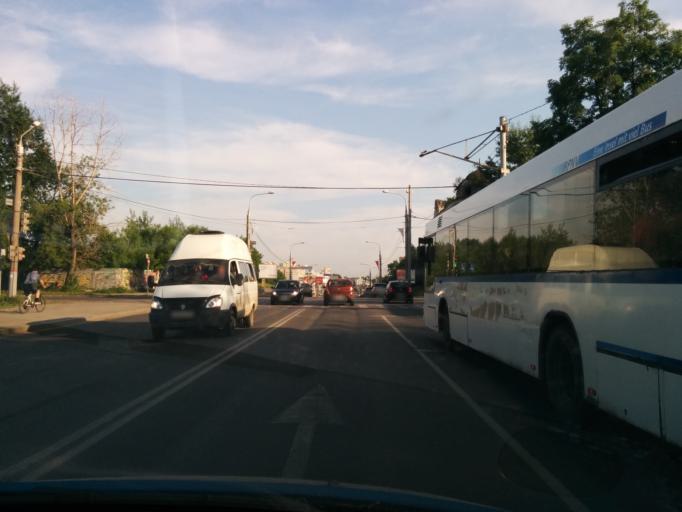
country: RU
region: Perm
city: Perm
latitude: 58.0141
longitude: 56.2239
